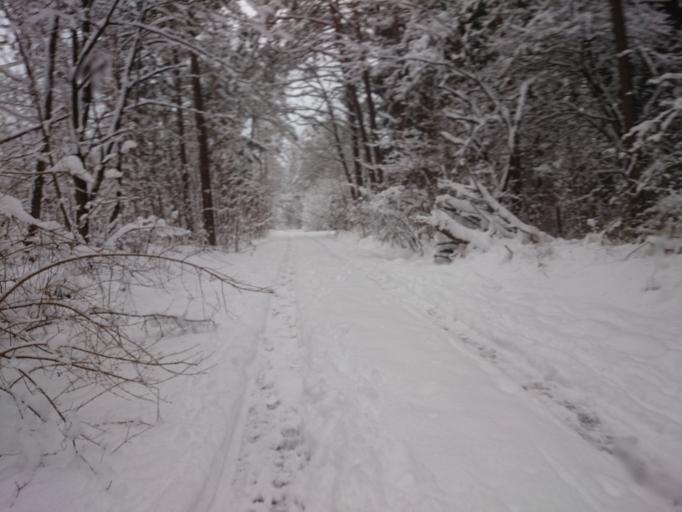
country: DE
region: Bavaria
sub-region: Swabia
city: Kissing
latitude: 48.2852
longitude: 10.9339
